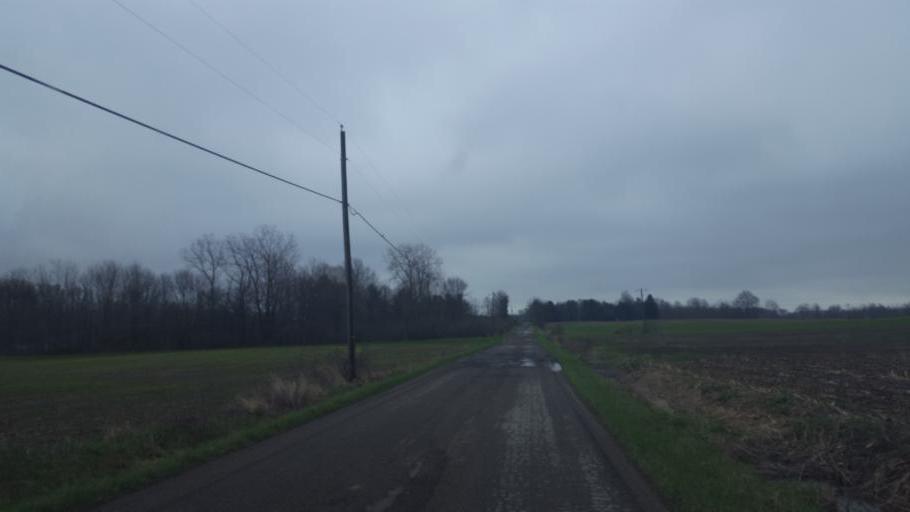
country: US
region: Ohio
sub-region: Crawford County
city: Galion
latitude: 40.6776
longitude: -82.7600
